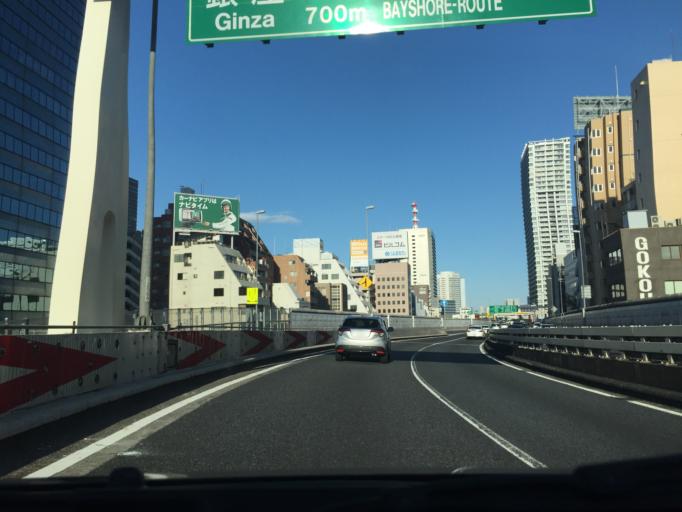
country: JP
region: Tokyo
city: Tokyo
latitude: 35.6536
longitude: 139.7509
